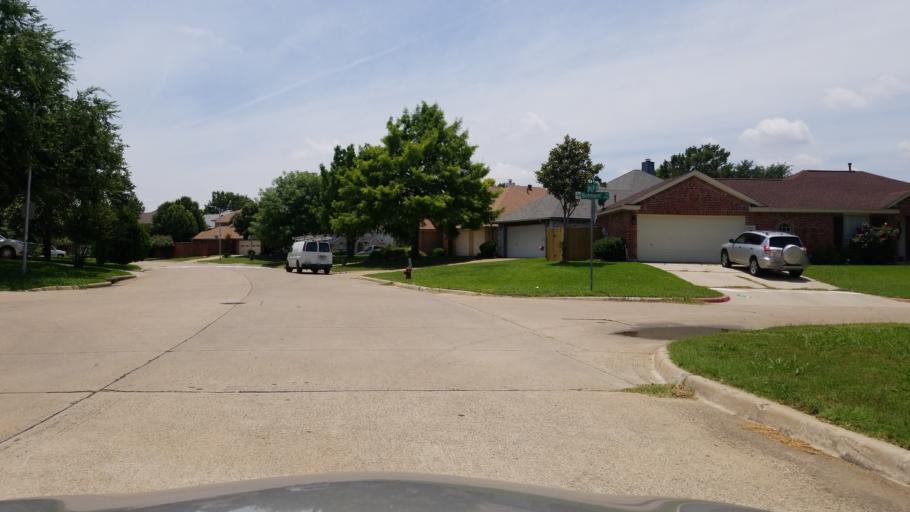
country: US
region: Texas
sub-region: Dallas County
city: Grand Prairie
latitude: 32.6801
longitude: -96.9903
